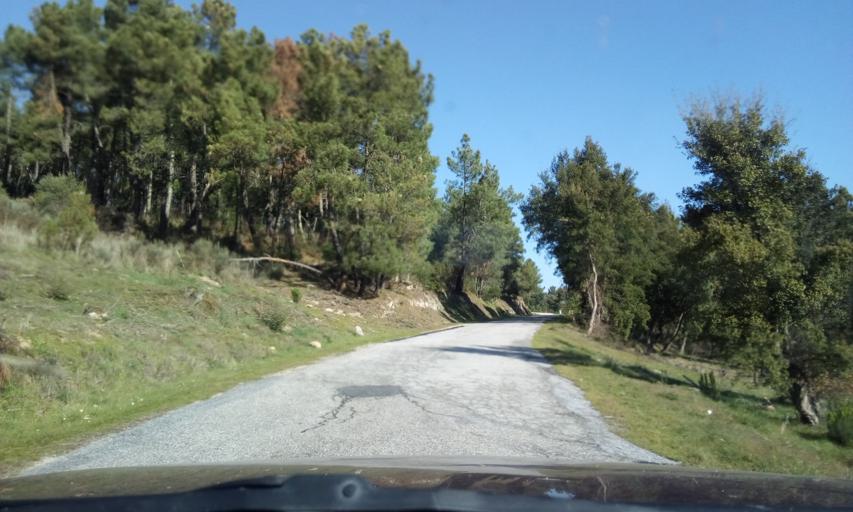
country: PT
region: Guarda
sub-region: Celorico da Beira
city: Celorico da Beira
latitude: 40.6923
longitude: -7.4537
